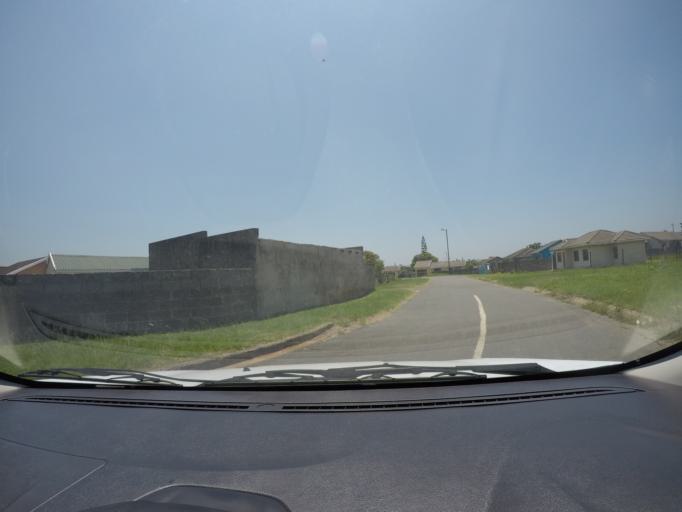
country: ZA
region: KwaZulu-Natal
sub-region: uThungulu District Municipality
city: eSikhawini
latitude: -28.8773
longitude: 31.8970
